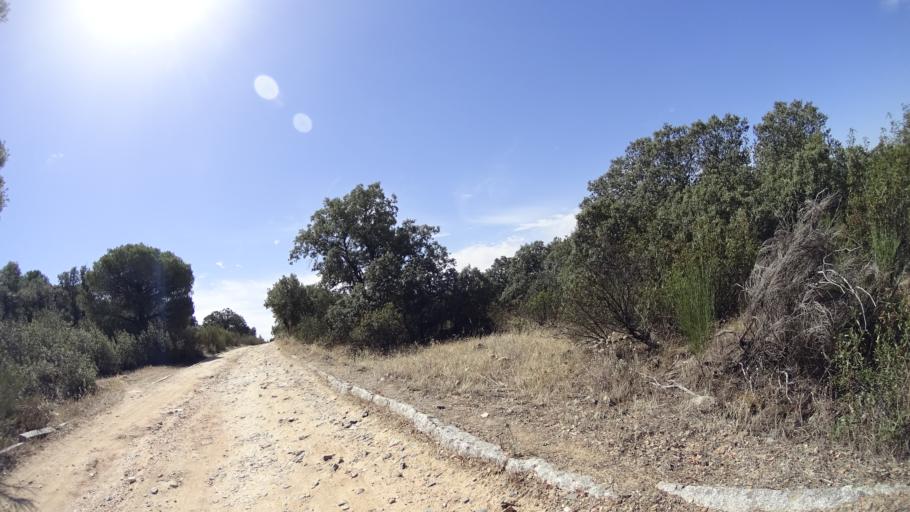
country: ES
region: Madrid
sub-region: Provincia de Madrid
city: Torrelodones
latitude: 40.5772
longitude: -3.9608
